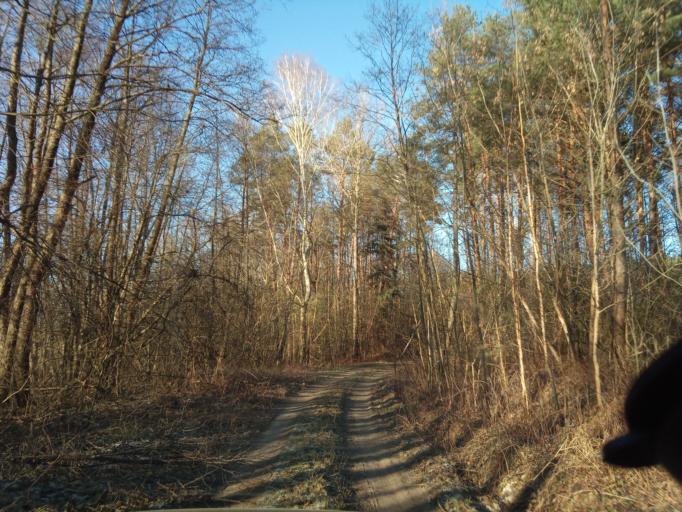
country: LT
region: Alytaus apskritis
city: Druskininkai
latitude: 53.9506
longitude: 23.8665
